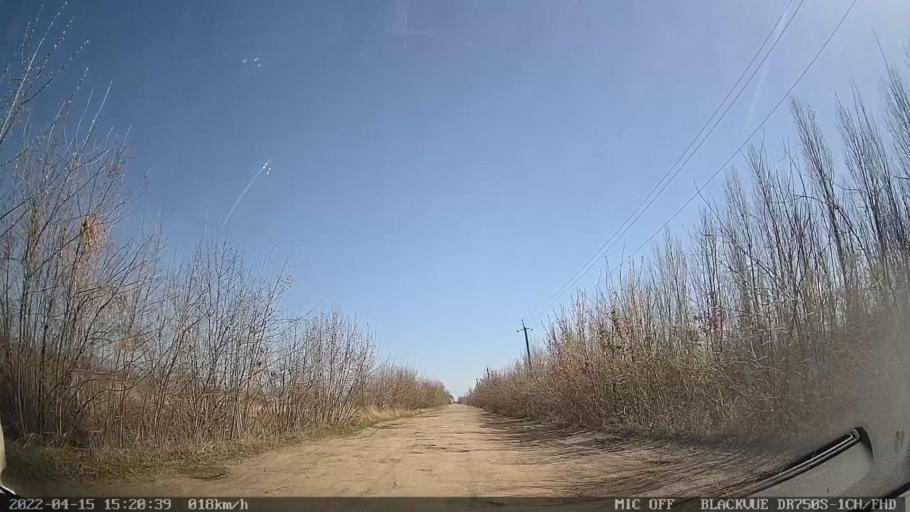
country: MD
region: Raionul Ocnita
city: Otaci
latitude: 48.3853
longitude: 27.9086
